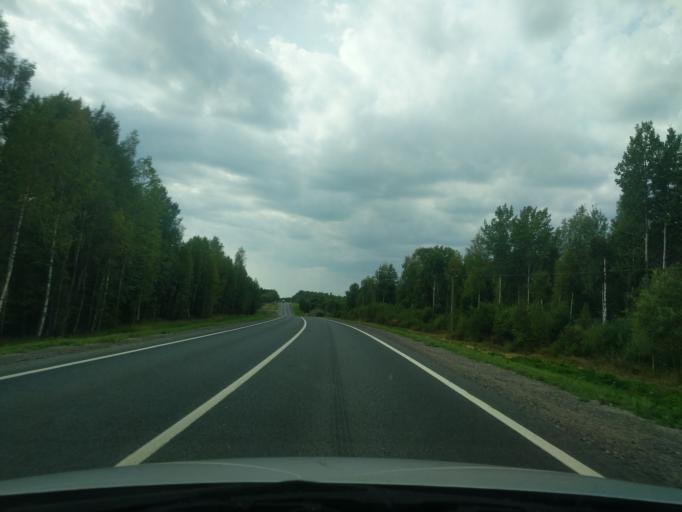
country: RU
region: Kostroma
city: Manturovo
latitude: 58.1651
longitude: 44.4043
